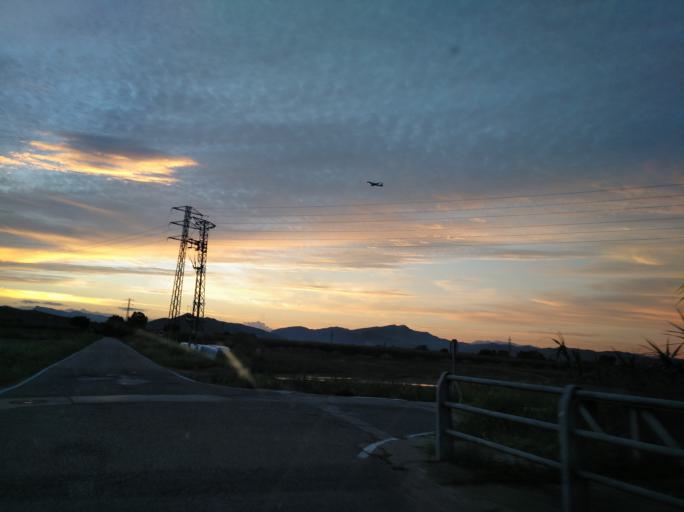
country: ES
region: Catalonia
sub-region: Provincia de Girona
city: Vilablareix
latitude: 41.9552
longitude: 2.7922
